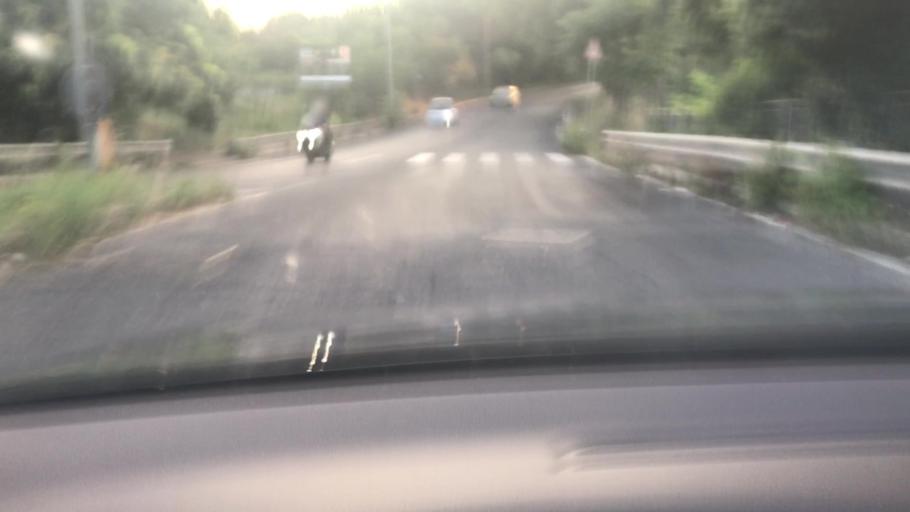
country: IT
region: Latium
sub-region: Citta metropolitana di Roma Capitale
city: Rome
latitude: 41.9243
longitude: 12.5677
